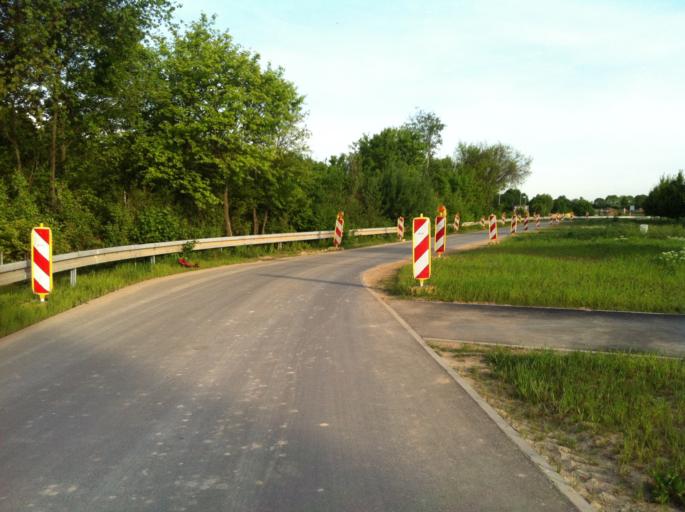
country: DE
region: Rheinland-Pfalz
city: Mainz
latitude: 49.9894
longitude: 8.2282
